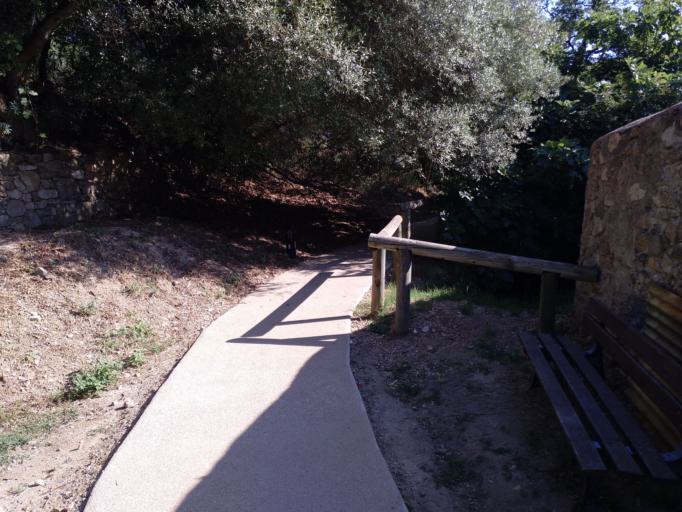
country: FR
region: Provence-Alpes-Cote d'Azur
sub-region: Departement du Var
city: Ramatuelle
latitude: 43.2162
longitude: 6.6127
